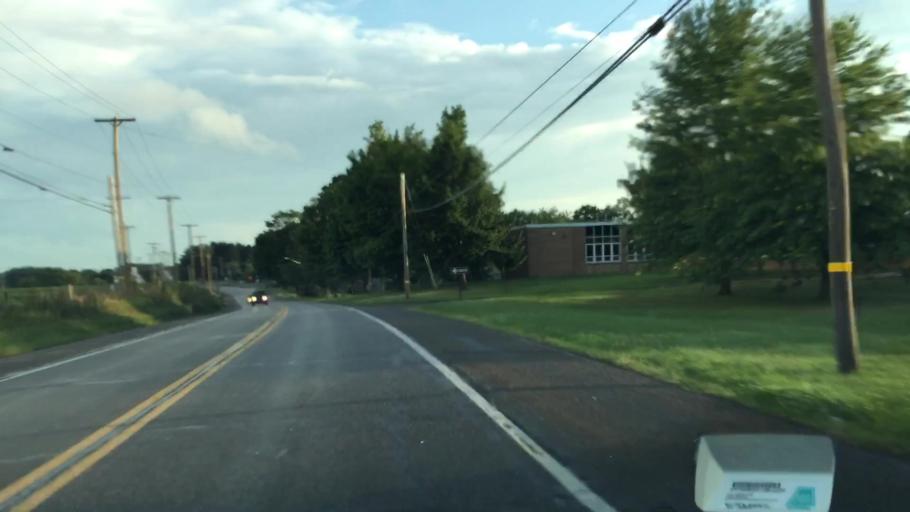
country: US
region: Pennsylvania
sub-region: Butler County
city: Meridian
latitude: 40.8257
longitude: -80.0109
